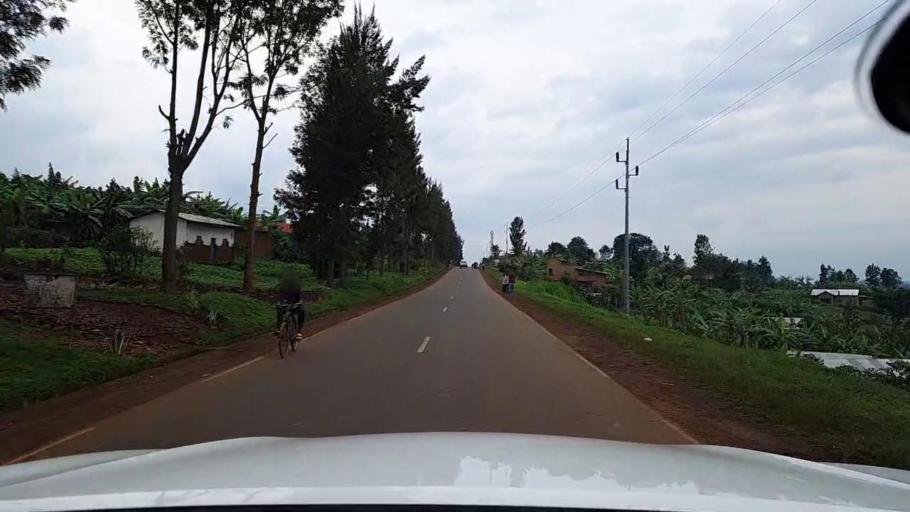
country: RW
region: Western Province
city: Cyangugu
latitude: -2.6225
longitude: 28.9471
